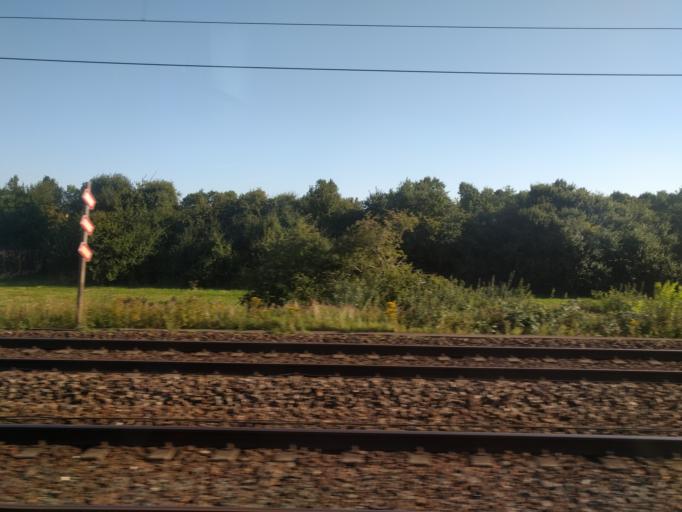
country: DK
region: Capital Region
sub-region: Hoje-Taastrup Kommune
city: Flong
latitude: 55.6463
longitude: 12.2114
